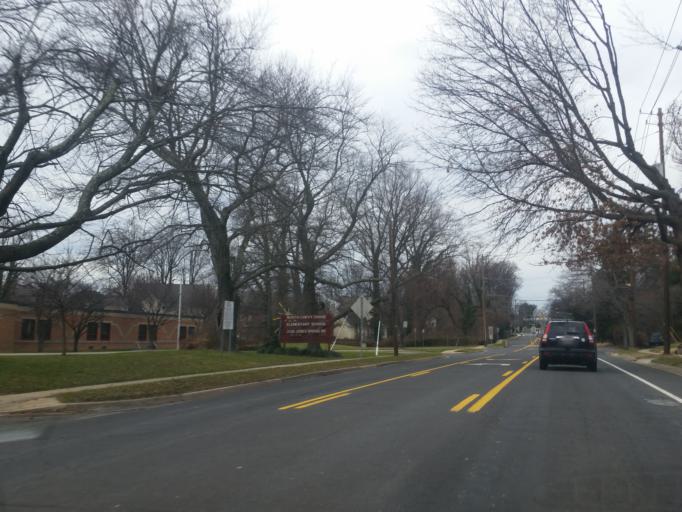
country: US
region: Maryland
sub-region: Montgomery County
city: South Kensington
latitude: 38.9994
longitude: -77.0732
